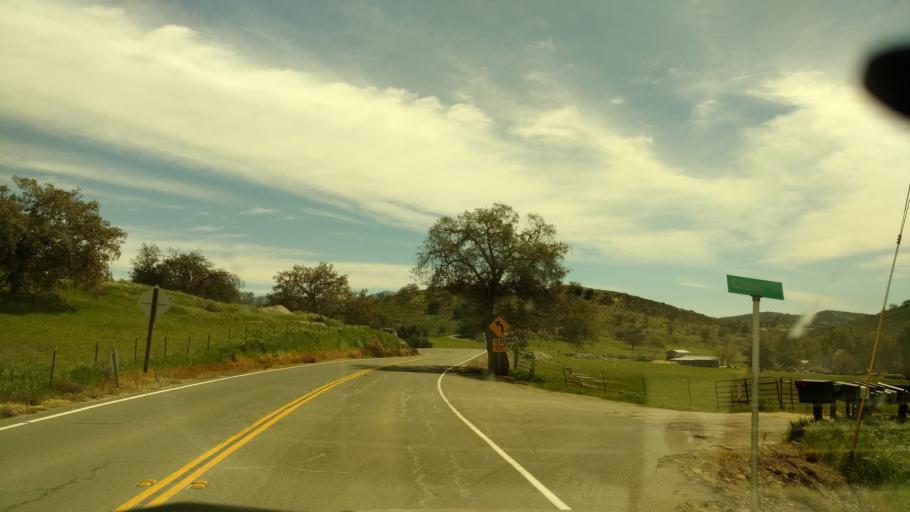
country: US
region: California
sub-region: San Diego County
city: San Diego Country Estates
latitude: 33.0723
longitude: -116.7680
